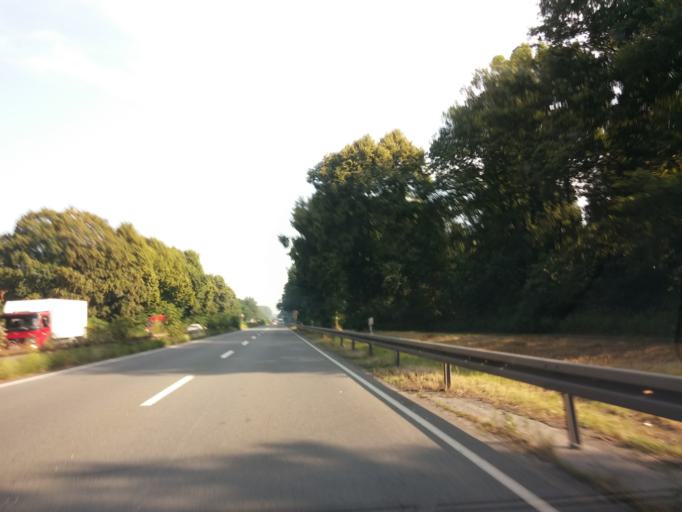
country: DE
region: North Rhine-Westphalia
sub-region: Regierungsbezirk Munster
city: Gladbeck
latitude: 51.5394
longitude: 6.9844
